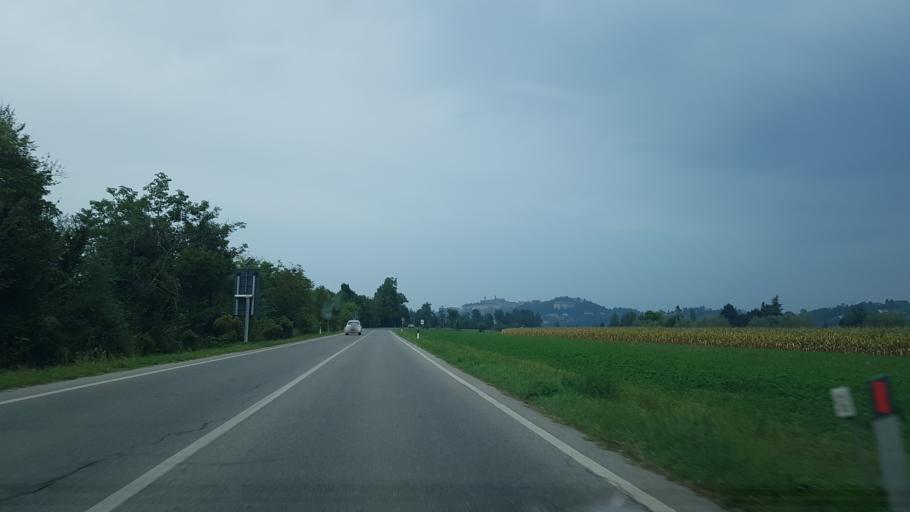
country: IT
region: Piedmont
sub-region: Provincia di Cuneo
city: Mondovi
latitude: 44.3688
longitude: 7.7991
